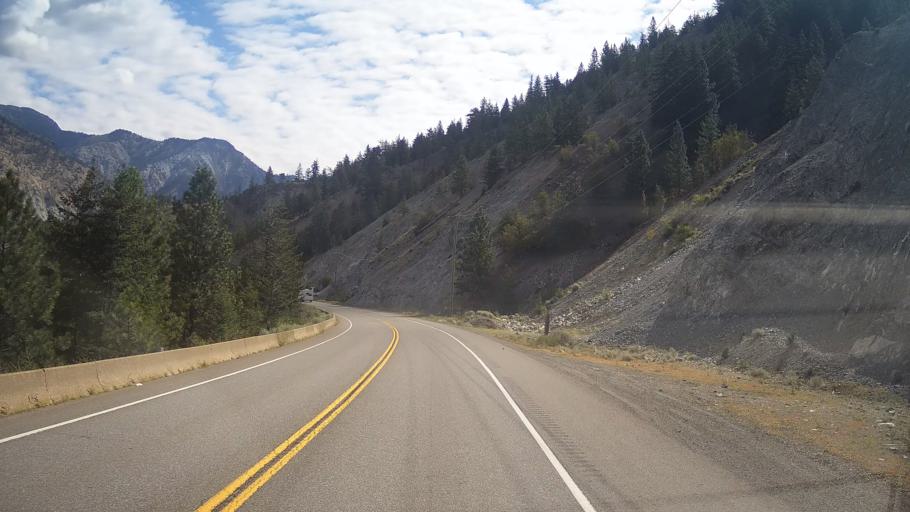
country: CA
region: British Columbia
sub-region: Thompson-Nicola Regional District
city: Ashcroft
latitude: 50.2504
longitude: -121.5517
